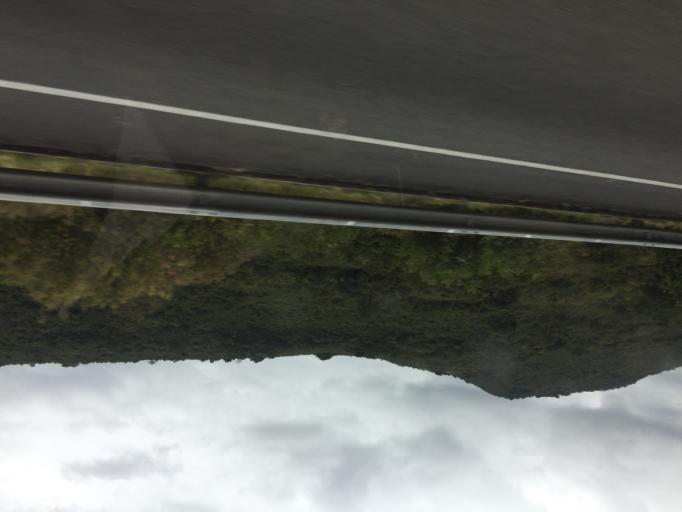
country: MX
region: Jalisco
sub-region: Zapotlan del Rey
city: Zapotlan del Rey
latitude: 20.5184
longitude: -102.9845
